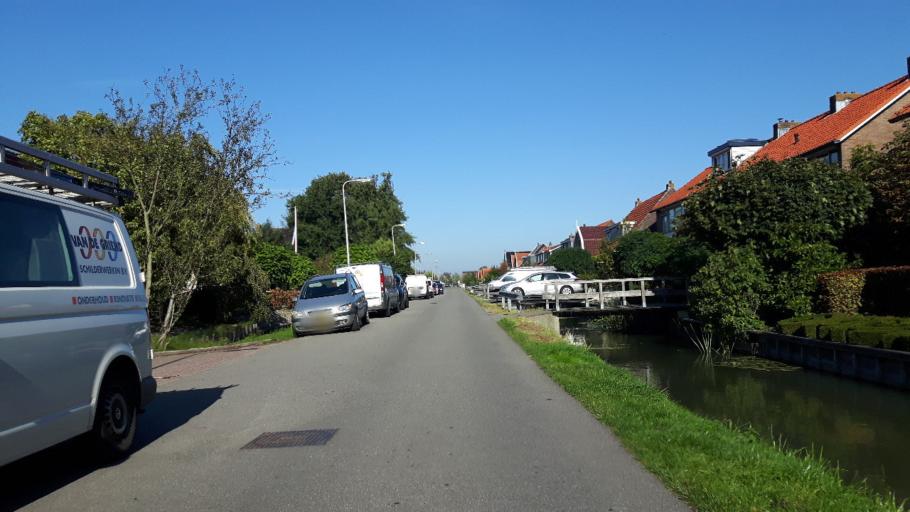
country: NL
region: South Holland
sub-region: Molenwaard
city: Liesveld
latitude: 51.9246
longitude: 4.7855
